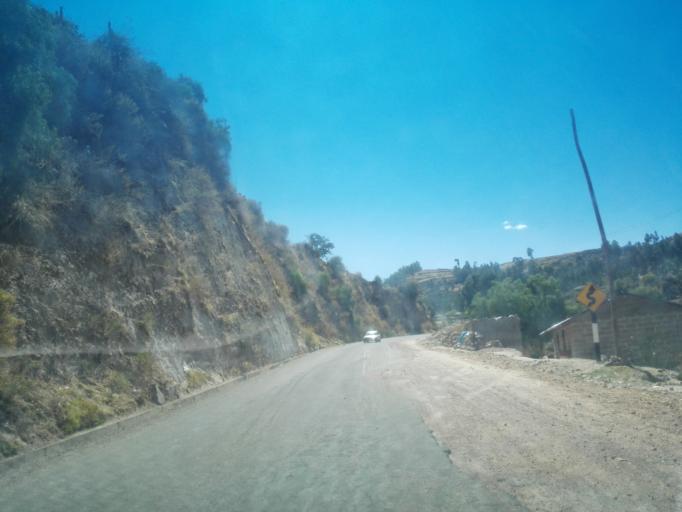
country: PE
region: Ayacucho
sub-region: Provincia de Huamanga
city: Ayacucho
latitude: -13.1655
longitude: -74.2464
